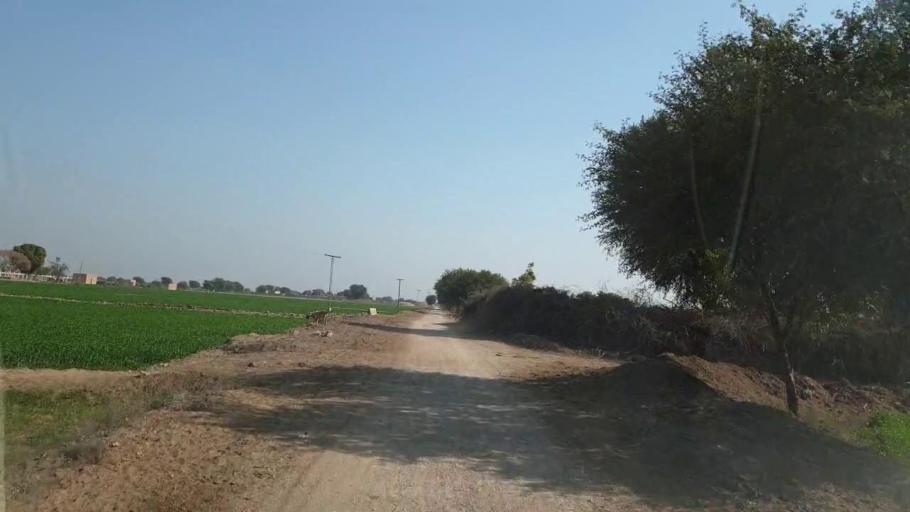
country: PK
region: Sindh
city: Tando Jam
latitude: 25.5078
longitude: 68.4901
